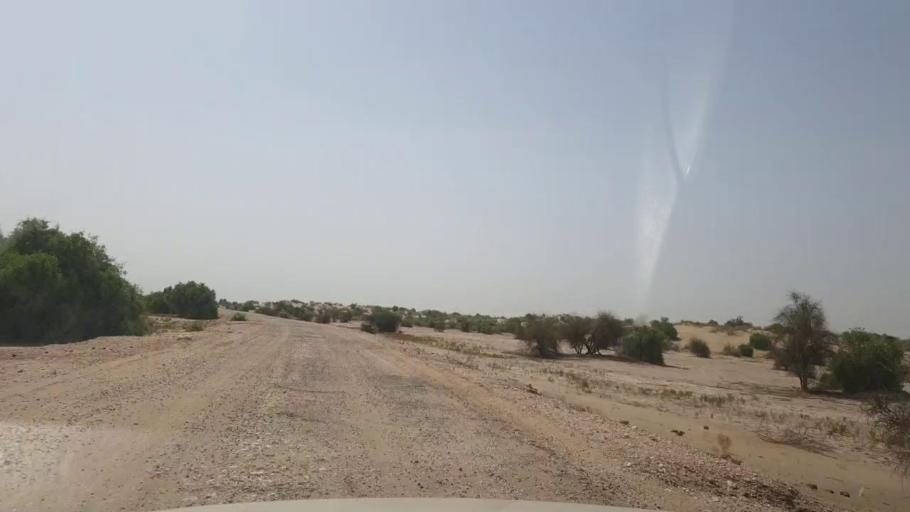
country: PK
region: Sindh
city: Rohri
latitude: 27.4374
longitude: 69.2449
